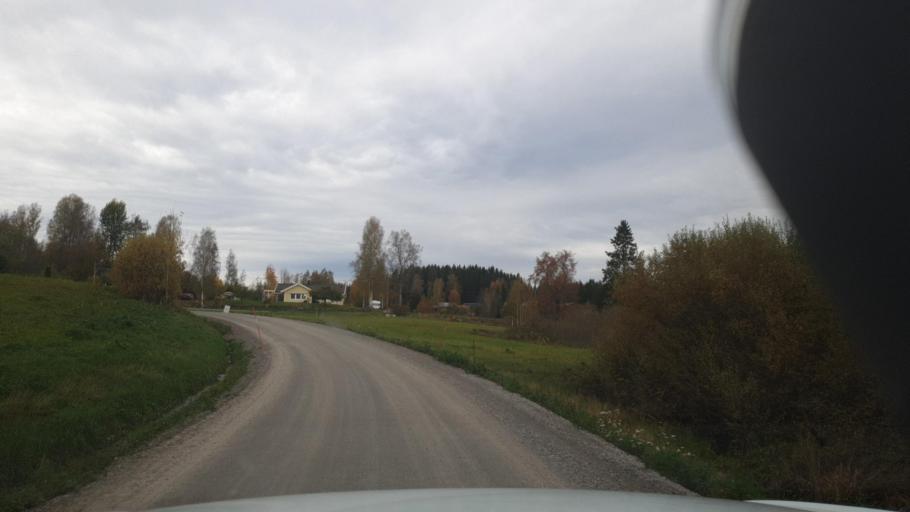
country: SE
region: Vaermland
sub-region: Arvika Kommun
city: Arvika
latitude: 59.6655
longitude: 12.7589
